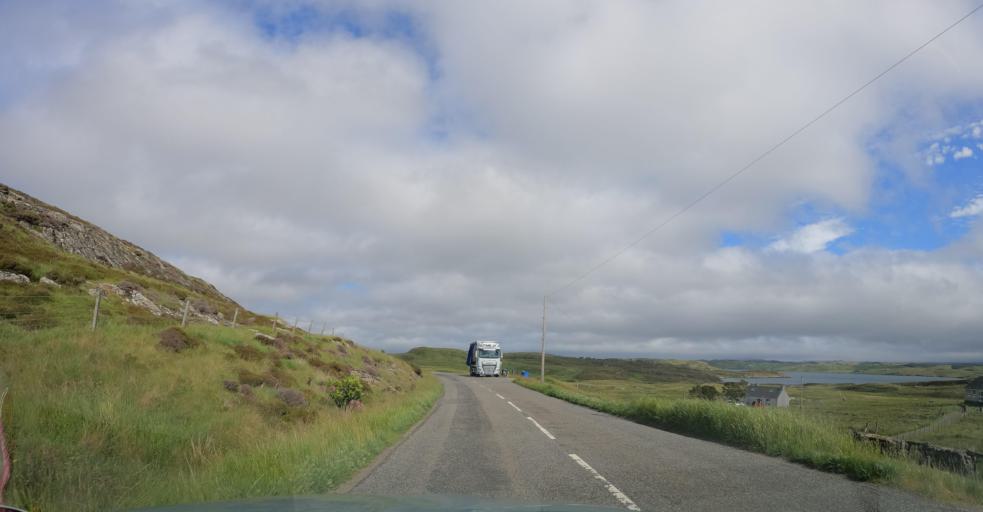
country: GB
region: Scotland
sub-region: Eilean Siar
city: Stornoway
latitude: 58.1056
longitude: -6.5206
